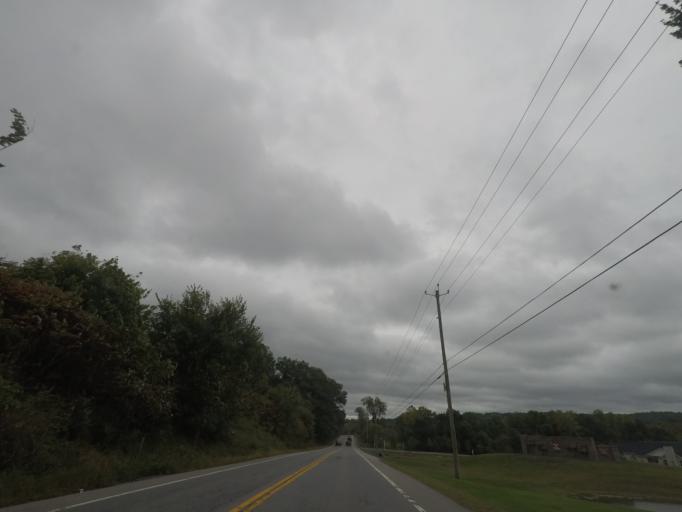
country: US
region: New York
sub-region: Saratoga County
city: Country Knolls
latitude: 42.9268
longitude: -73.7602
